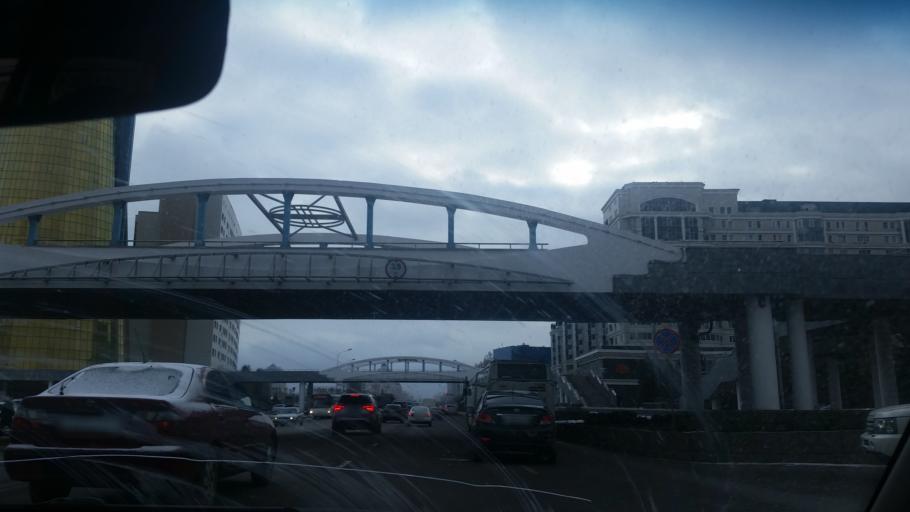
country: KZ
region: Astana Qalasy
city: Astana
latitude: 51.1278
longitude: 71.4386
